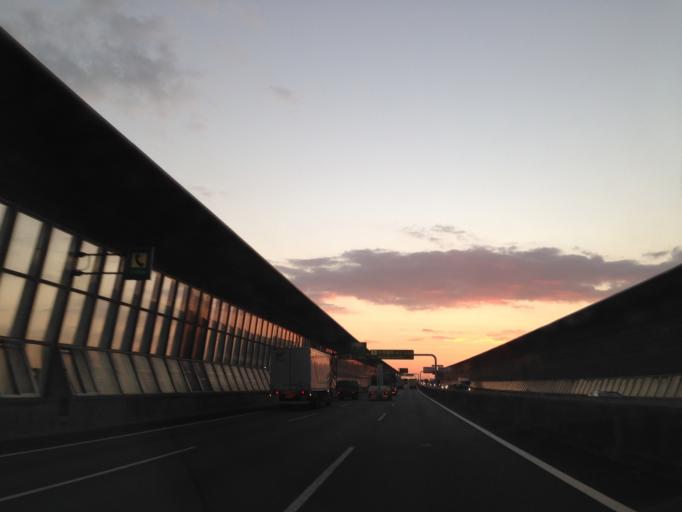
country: JP
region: Aichi
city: Obu
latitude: 35.0476
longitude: 136.9155
